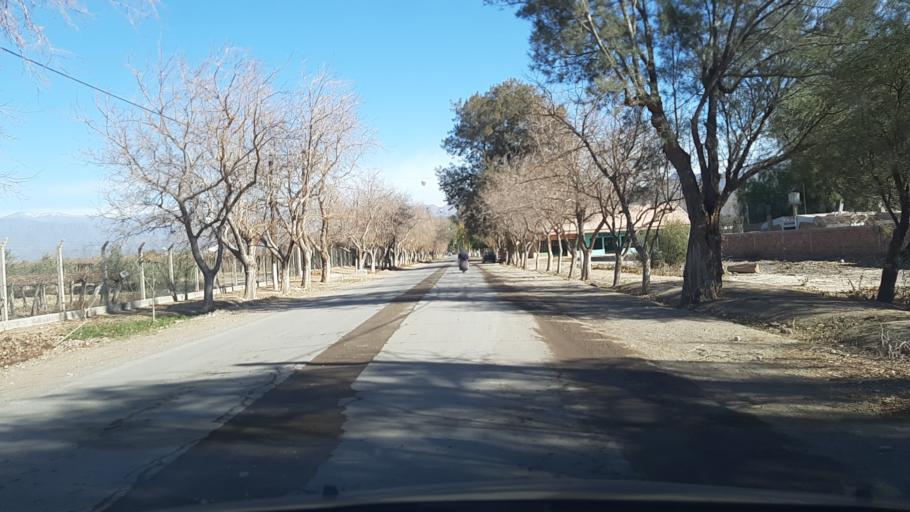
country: AR
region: San Juan
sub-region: Departamento de Zonda
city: Zonda
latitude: -31.4609
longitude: -68.7289
